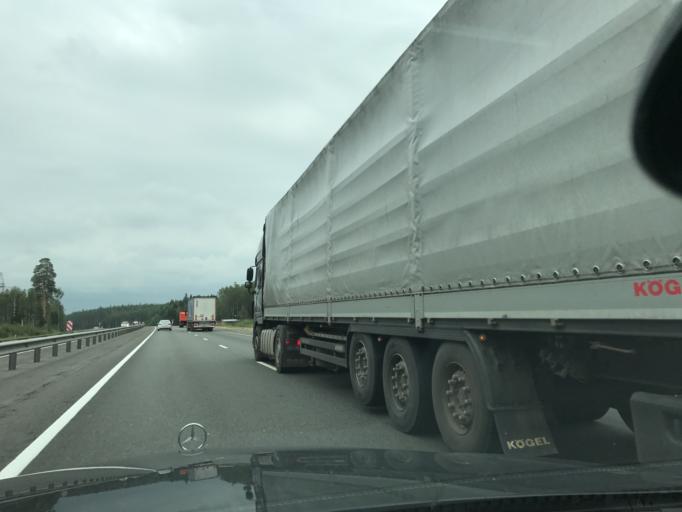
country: RU
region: Vladimir
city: Kameshkovo
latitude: 56.1722
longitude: 40.9414
